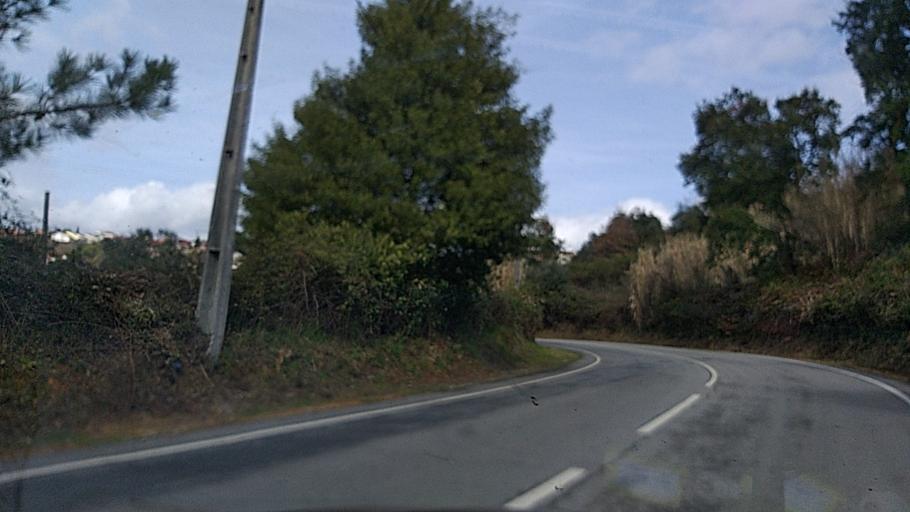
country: PT
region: Viseu
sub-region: Satao
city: Satao
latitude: 40.6710
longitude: -7.6945
